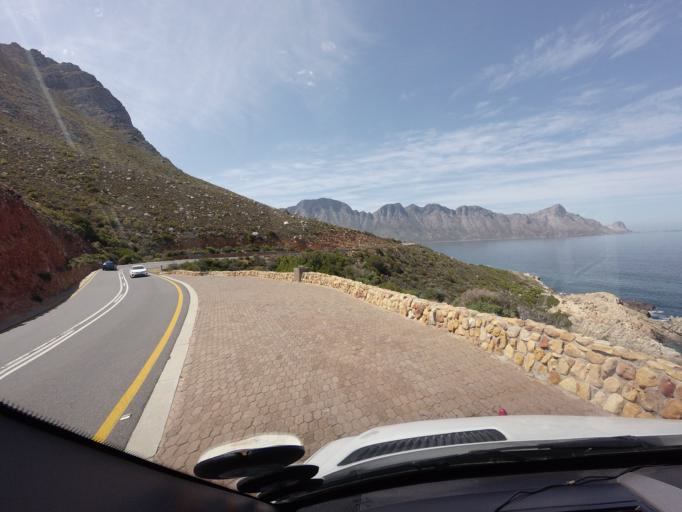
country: ZA
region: Western Cape
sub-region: Overberg District Municipality
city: Grabouw
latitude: -34.2189
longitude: 18.8338
